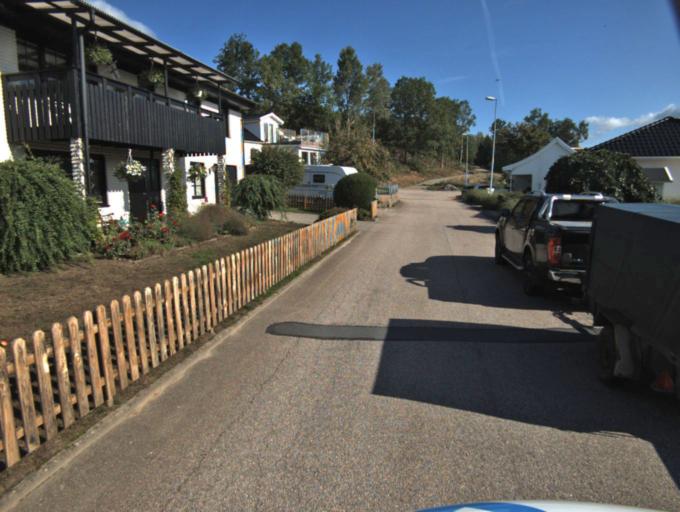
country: SE
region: Vaestra Goetaland
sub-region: Ulricehamns Kommun
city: Ulricehamn
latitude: 57.8053
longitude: 13.3984
